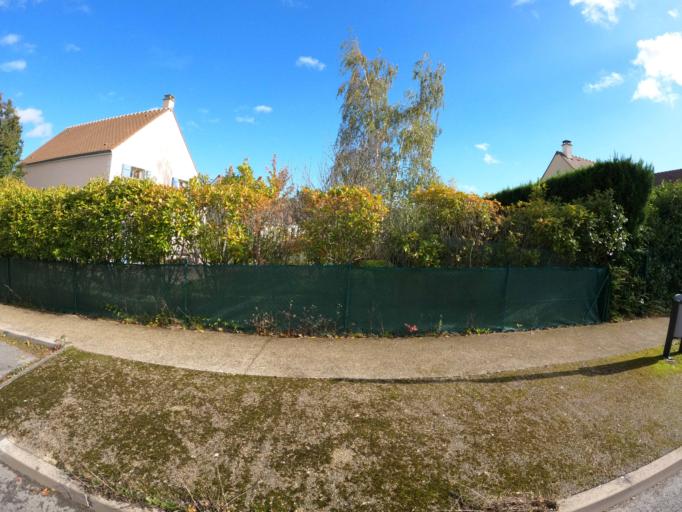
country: FR
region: Ile-de-France
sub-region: Departement de Seine-et-Marne
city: Esbly
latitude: 48.8897
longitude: 2.8138
